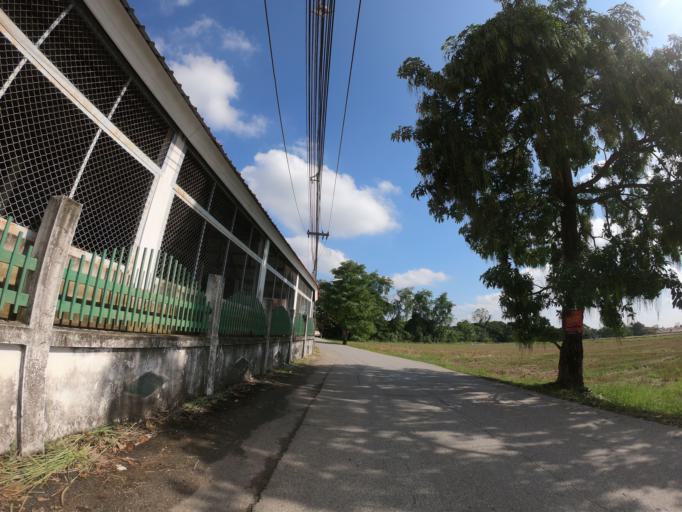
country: TH
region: Chiang Mai
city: San Sai
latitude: 18.8491
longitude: 99.0476
